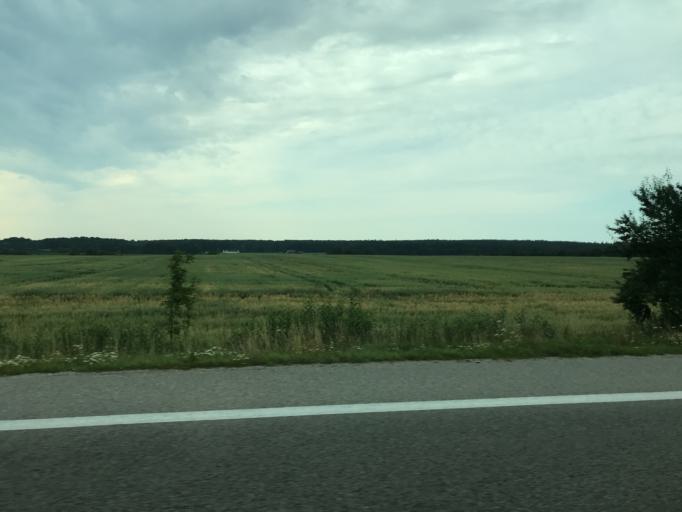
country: CZ
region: Jihocesky
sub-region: Okres Jindrichuv Hradec
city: Trebon
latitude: 48.9996
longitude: 14.7335
